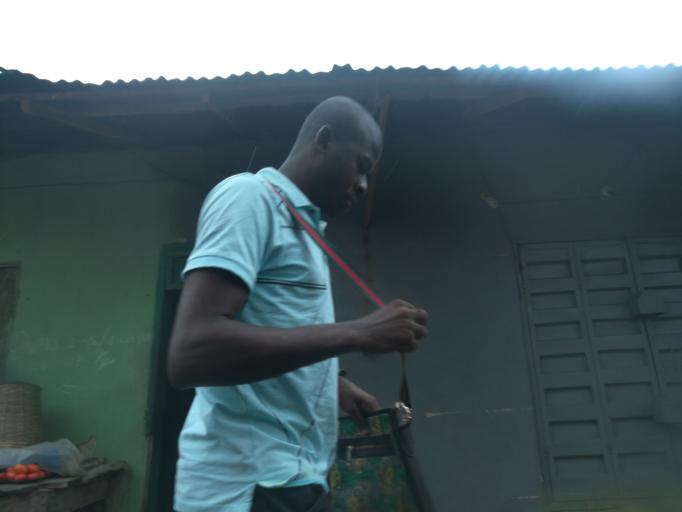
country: NG
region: Lagos
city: Oshodi
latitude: 6.5750
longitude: 3.3433
